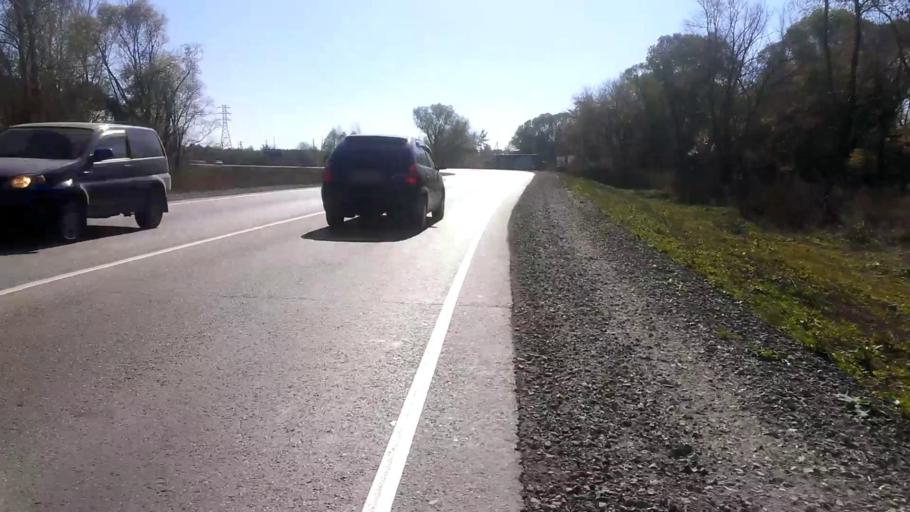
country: RU
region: Altai Krai
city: Sannikovo
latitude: 53.3228
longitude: 83.9429
